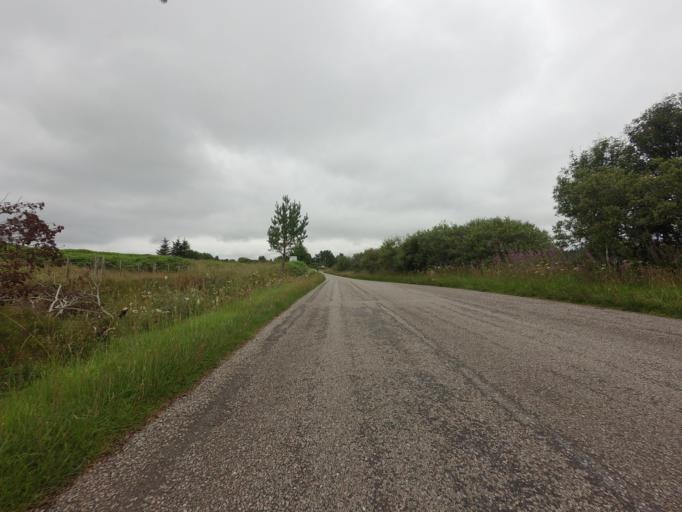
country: GB
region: Scotland
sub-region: Highland
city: Alness
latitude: 58.0105
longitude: -4.4029
